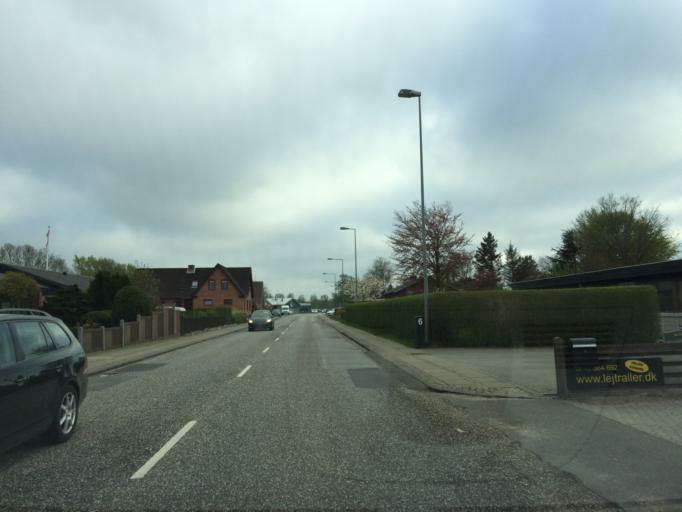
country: DK
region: Central Jutland
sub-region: Herning Kommune
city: Avlum
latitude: 56.2600
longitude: 8.7930
